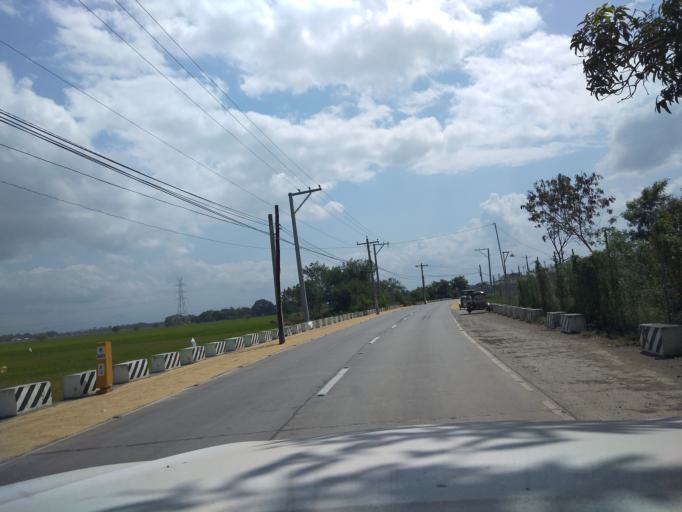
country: PH
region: Central Luzon
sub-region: Province of Pampanga
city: Talang
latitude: 15.0237
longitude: 120.8445
